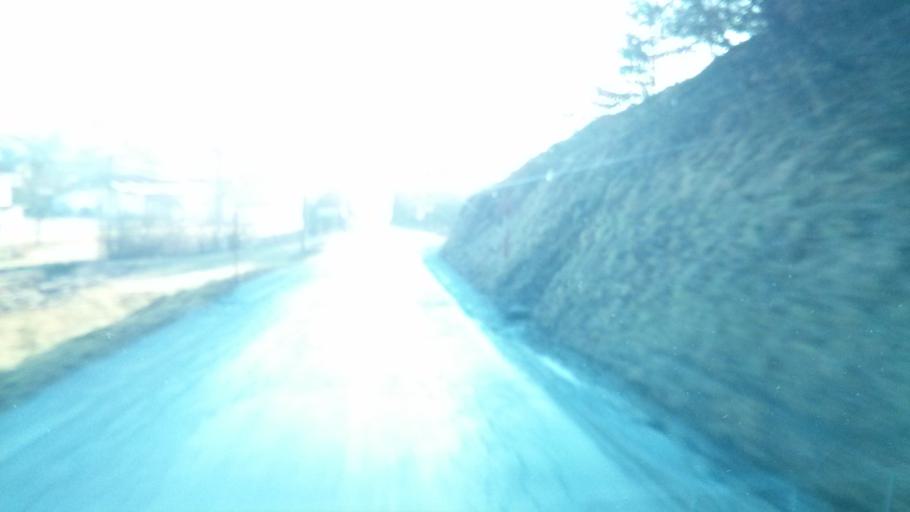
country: SI
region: Trebnje
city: Mirna
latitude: 45.9995
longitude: 14.9812
